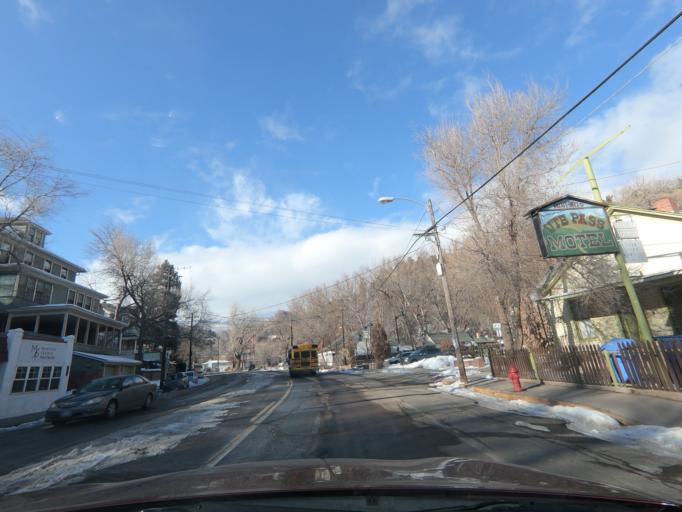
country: US
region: Colorado
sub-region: El Paso County
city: Manitou Springs
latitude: 38.8613
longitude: -104.9211
